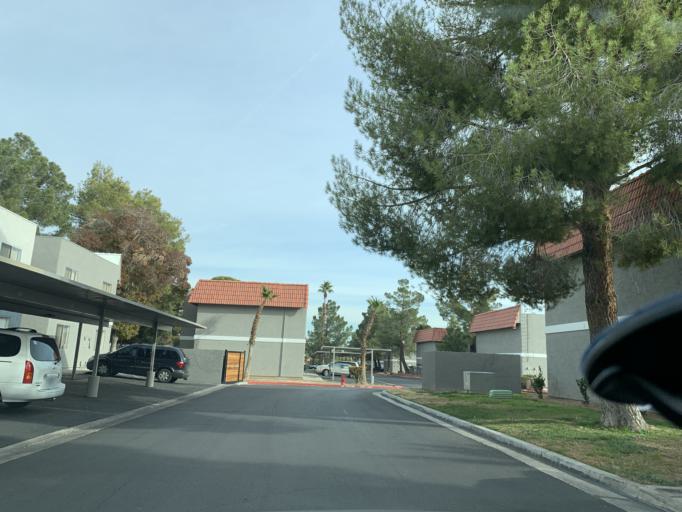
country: US
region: Nevada
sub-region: Clark County
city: Spring Valley
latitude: 36.0979
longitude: -115.2274
